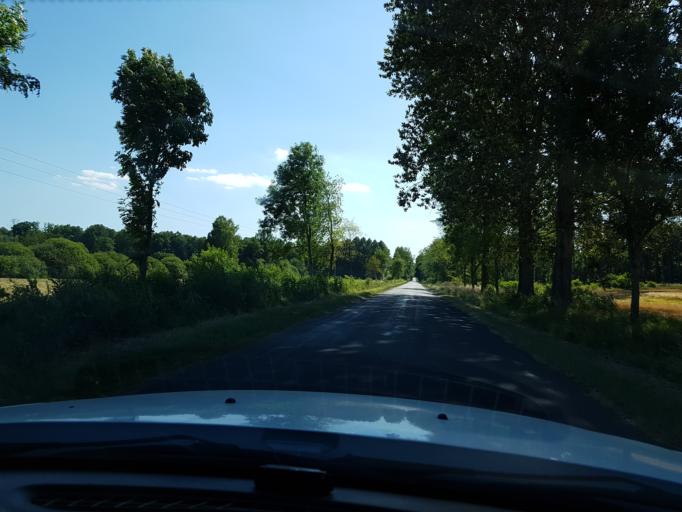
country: PL
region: West Pomeranian Voivodeship
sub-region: Powiat bialogardzki
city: Karlino
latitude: 53.9523
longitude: 15.8671
